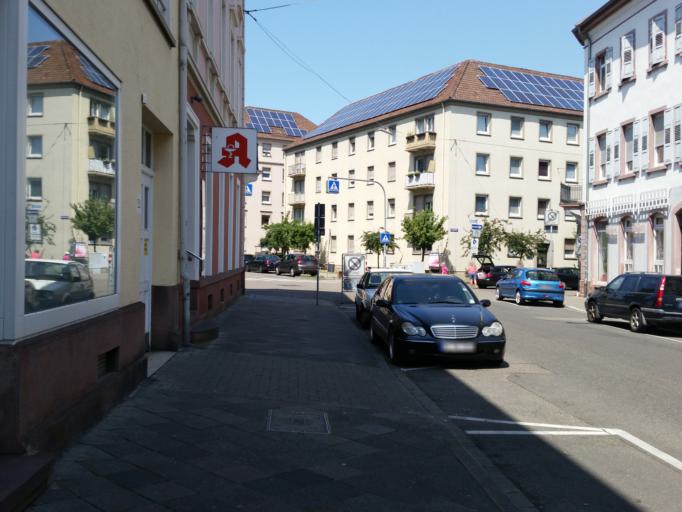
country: DE
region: Baden-Wuerttemberg
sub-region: Karlsruhe Region
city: Karlsruhe
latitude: 49.0074
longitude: 8.3900
